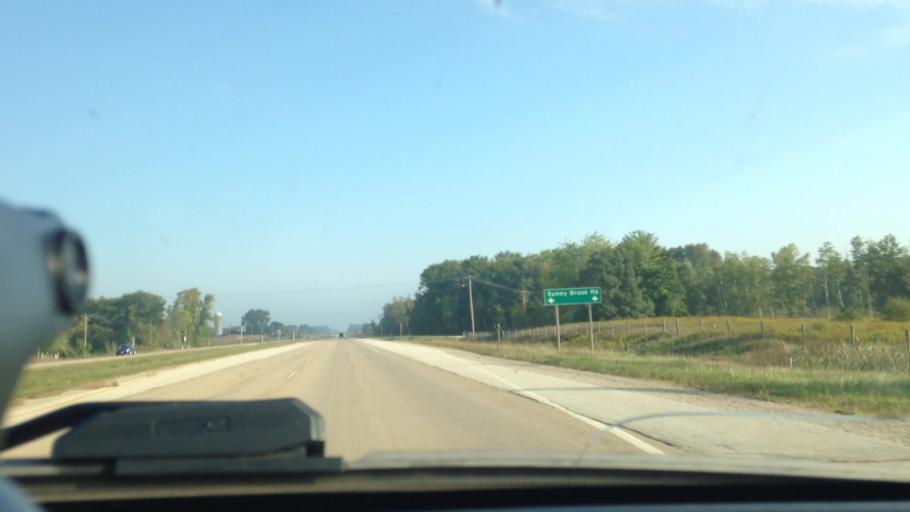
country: US
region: Wisconsin
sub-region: Oconto County
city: Oconto Falls
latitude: 44.9994
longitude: -88.0450
